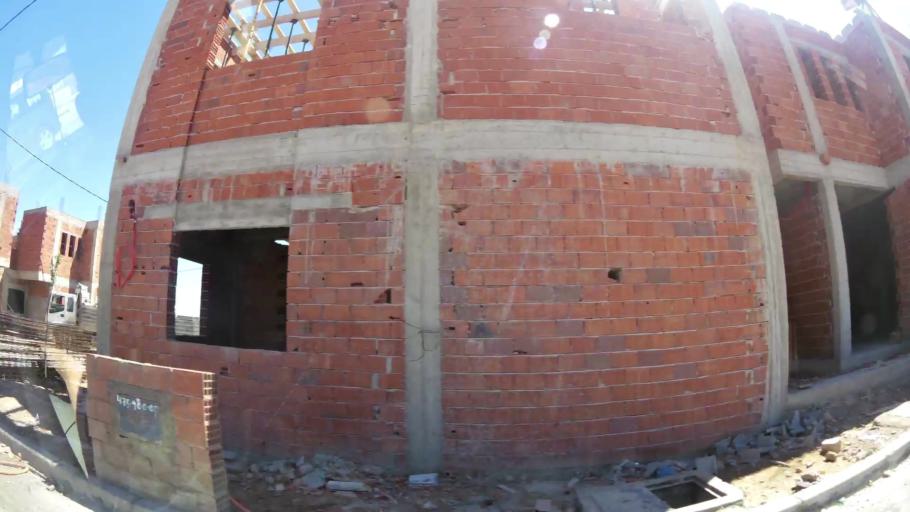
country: MA
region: Oriental
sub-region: Oujda-Angad
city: Oujda
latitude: 34.6500
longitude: -1.8776
